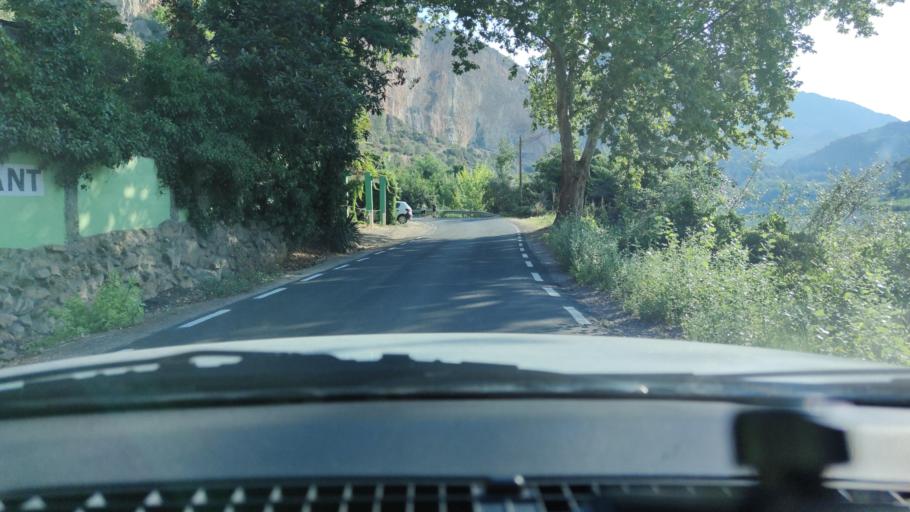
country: ES
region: Catalonia
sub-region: Provincia de Lleida
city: Camarasa
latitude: 41.8719
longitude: 0.8430
